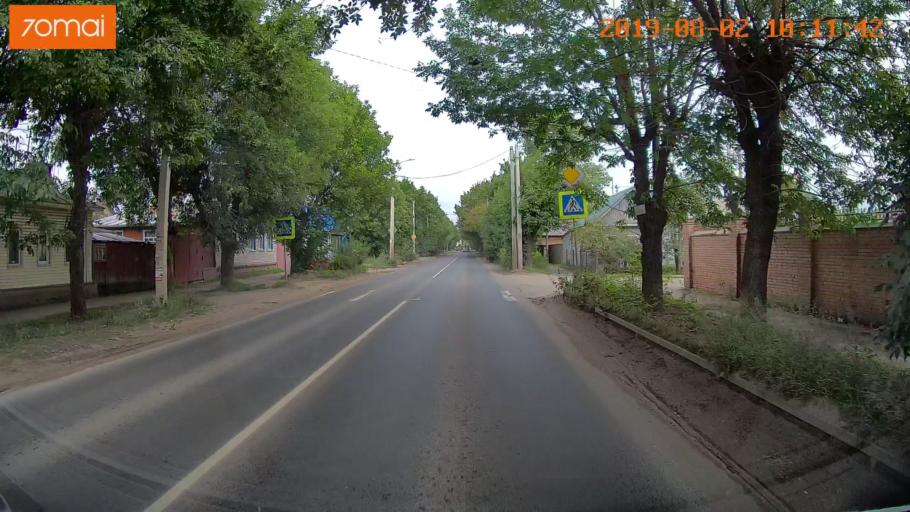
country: RU
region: Ivanovo
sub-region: Gorod Ivanovo
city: Ivanovo
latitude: 56.9945
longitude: 40.9520
